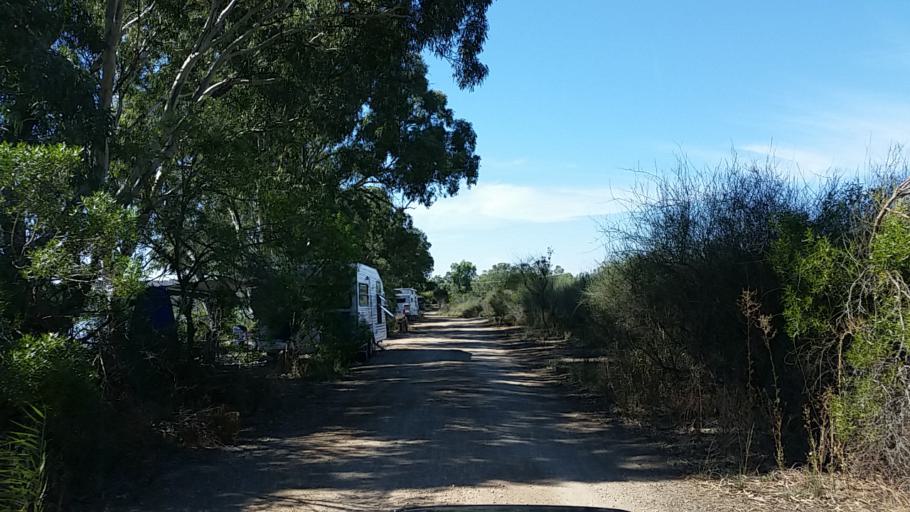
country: AU
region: South Australia
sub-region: Mid Murray
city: Mannum
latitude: -34.7500
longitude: 139.5540
